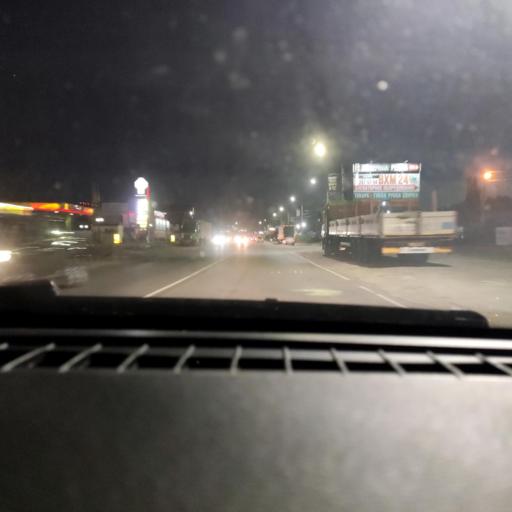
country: RU
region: Voronezj
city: Maslovka
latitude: 51.6436
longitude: 39.2958
